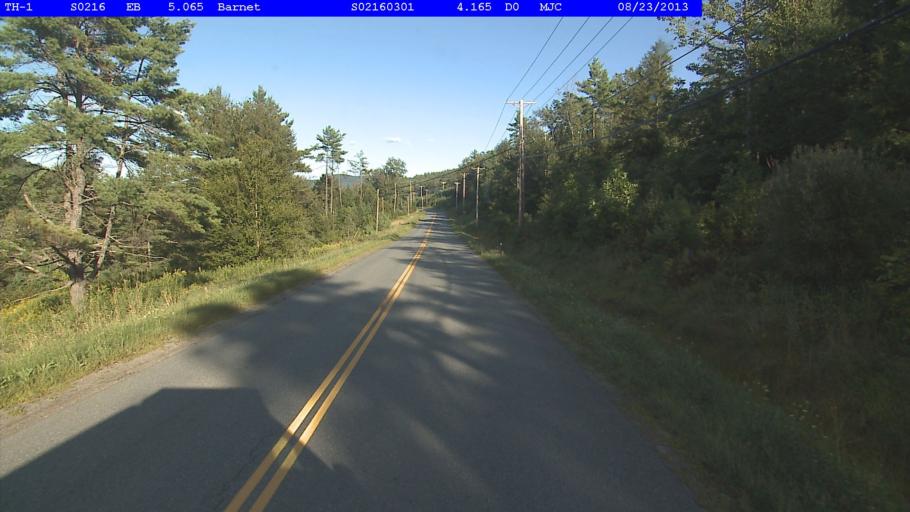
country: US
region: Vermont
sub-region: Caledonia County
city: Saint Johnsbury
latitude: 44.3018
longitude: -72.0773
